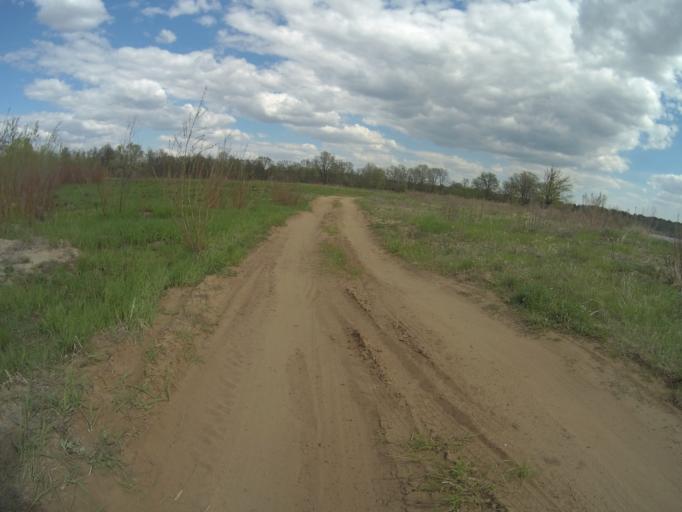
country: RU
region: Vladimir
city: Kommunar
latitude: 56.0860
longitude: 40.4178
